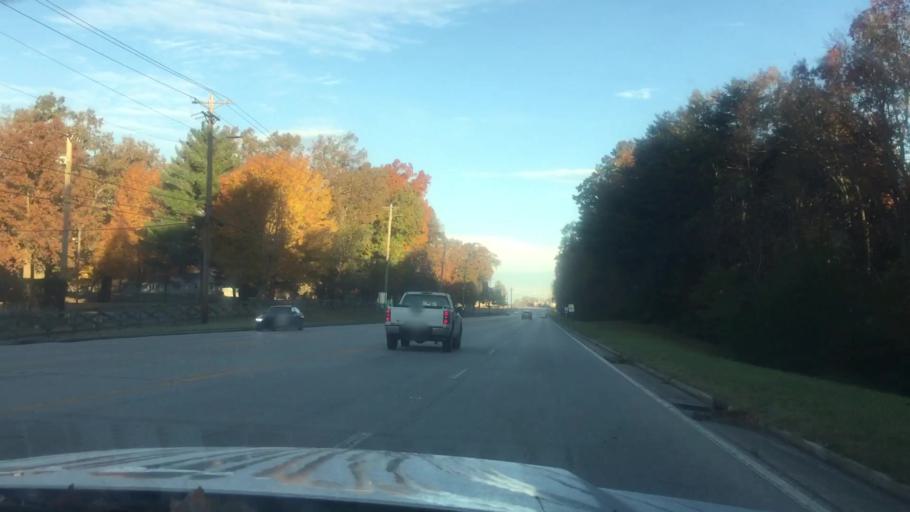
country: US
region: Tennessee
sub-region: Coffee County
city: Tullahoma
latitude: 35.3404
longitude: -86.1903
